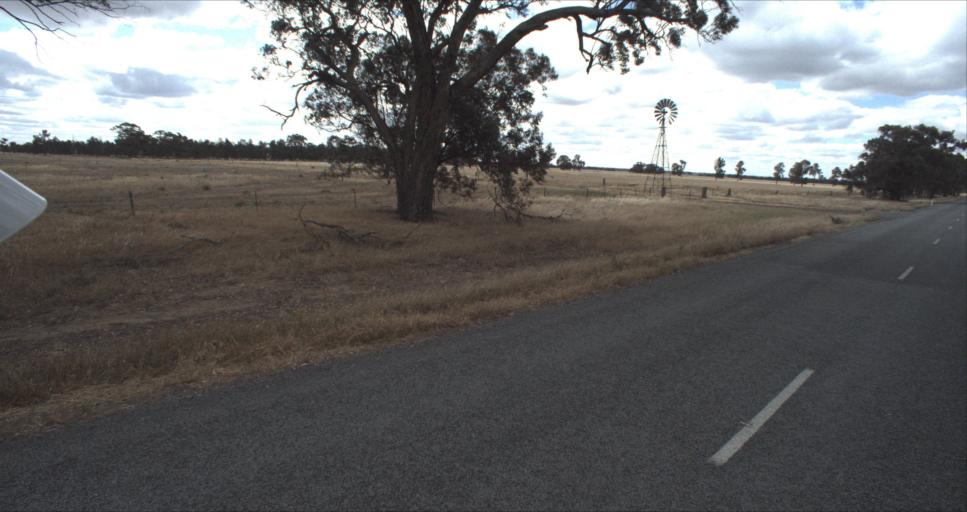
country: AU
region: New South Wales
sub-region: Leeton
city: Leeton
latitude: -34.6870
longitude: 146.3445
